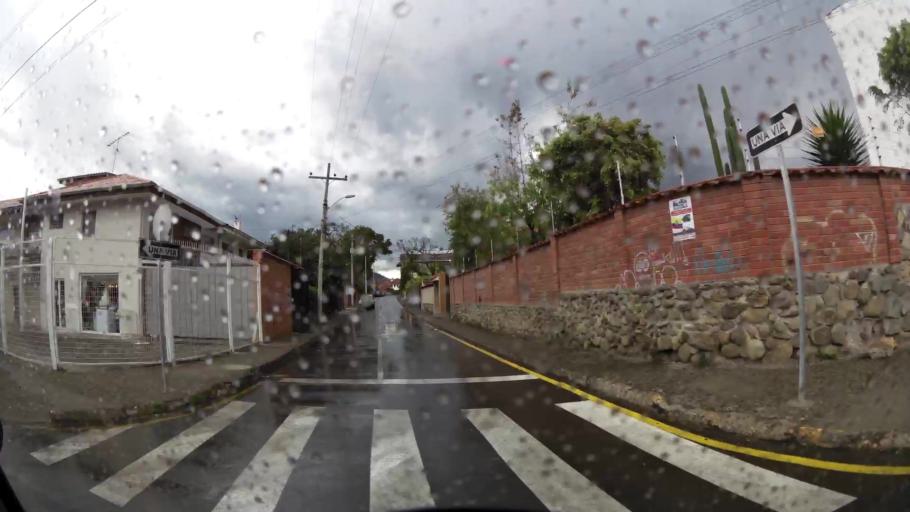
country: EC
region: Azuay
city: Cuenca
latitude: -2.8993
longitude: -79.0168
